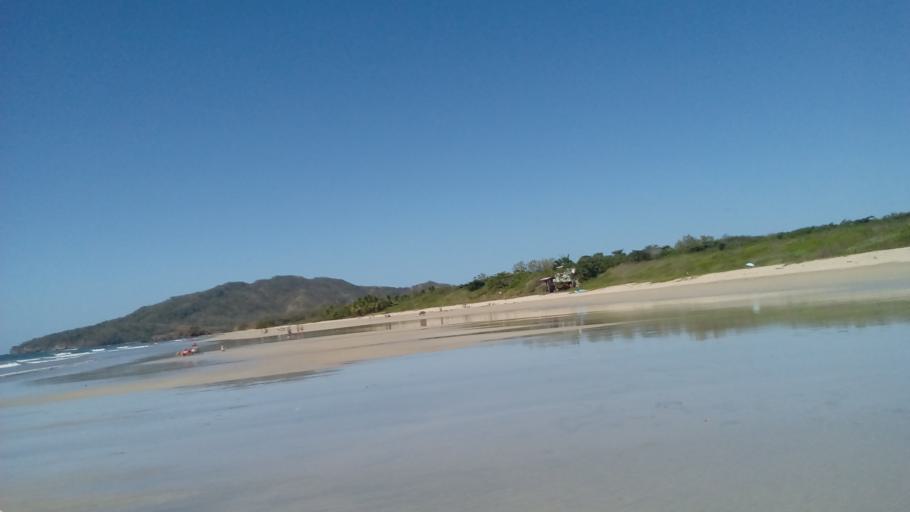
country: CR
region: Guanacaste
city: Belen
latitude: 10.3318
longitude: -85.8474
